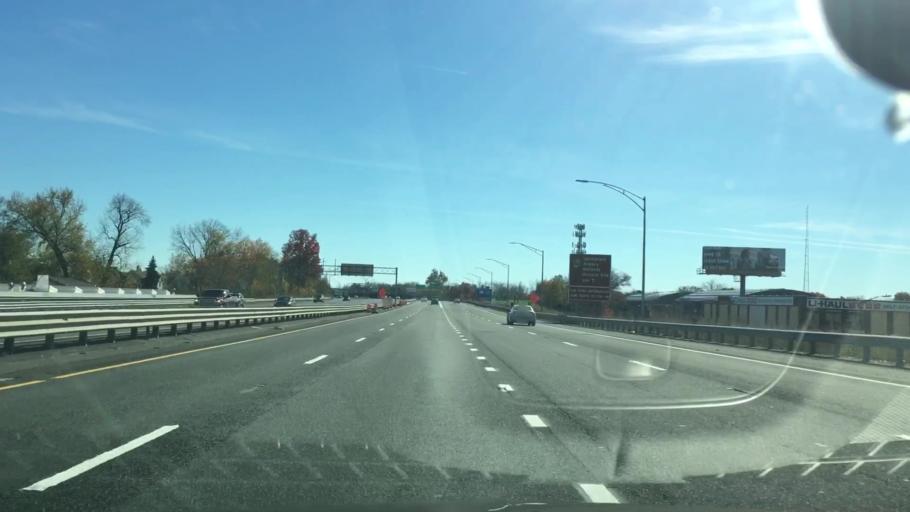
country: US
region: Massachusetts
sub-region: Hampden County
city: West Springfield
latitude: 42.1172
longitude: -72.6093
